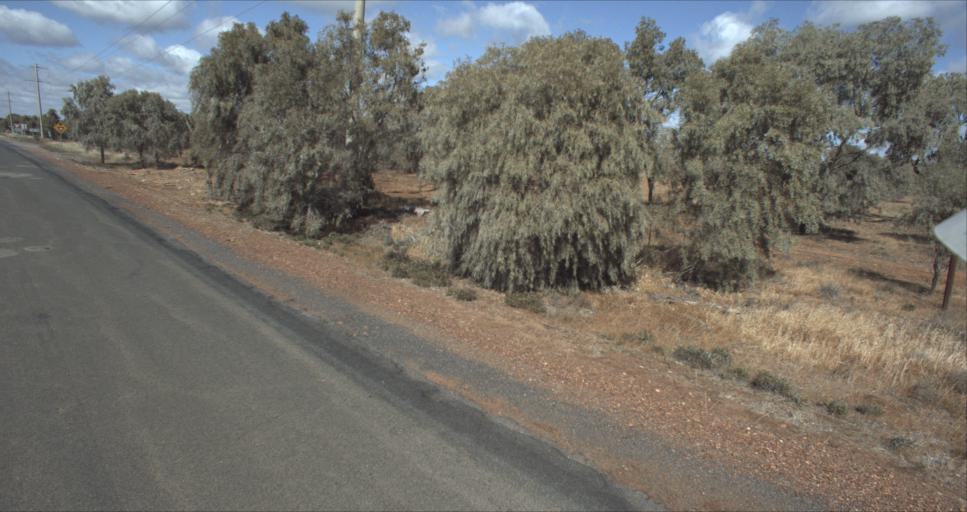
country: AU
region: New South Wales
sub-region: Murrumbidgee Shire
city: Darlington Point
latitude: -34.5156
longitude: 146.1767
